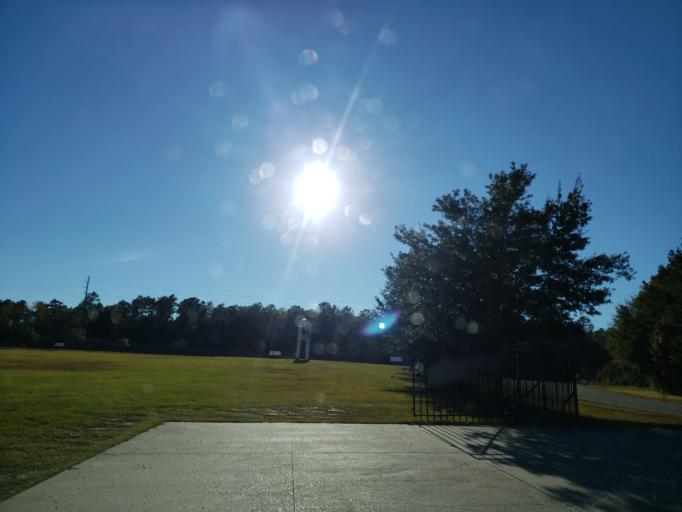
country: US
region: Mississippi
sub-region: Forrest County
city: Hattiesburg
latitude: 31.2560
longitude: -89.2788
